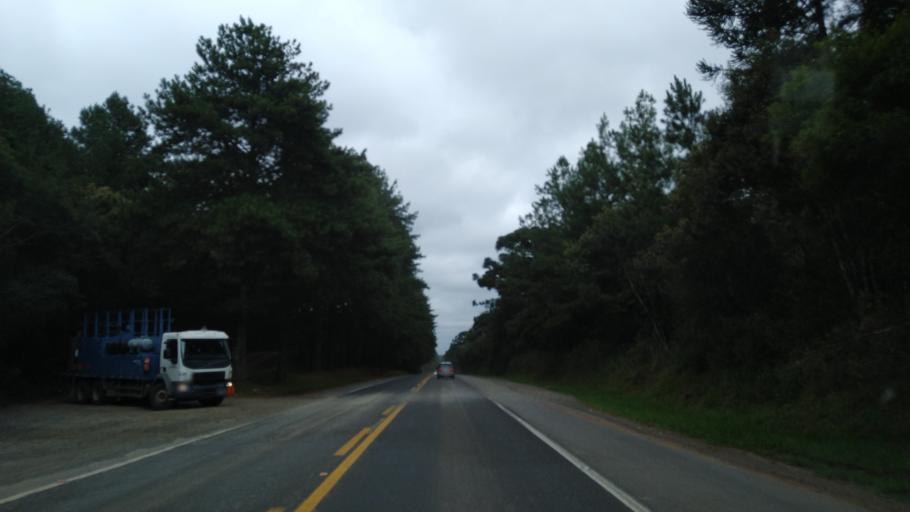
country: BR
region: Santa Catarina
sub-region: Tres Barras
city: Tres Barras
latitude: -26.1639
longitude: -50.1200
